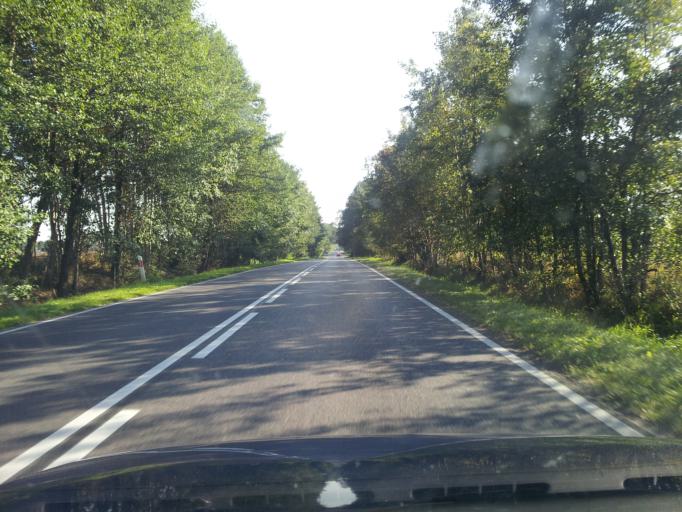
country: PL
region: Masovian Voivodeship
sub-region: Powiat warszawski zachodni
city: Leszno
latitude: 52.2907
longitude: 20.6019
